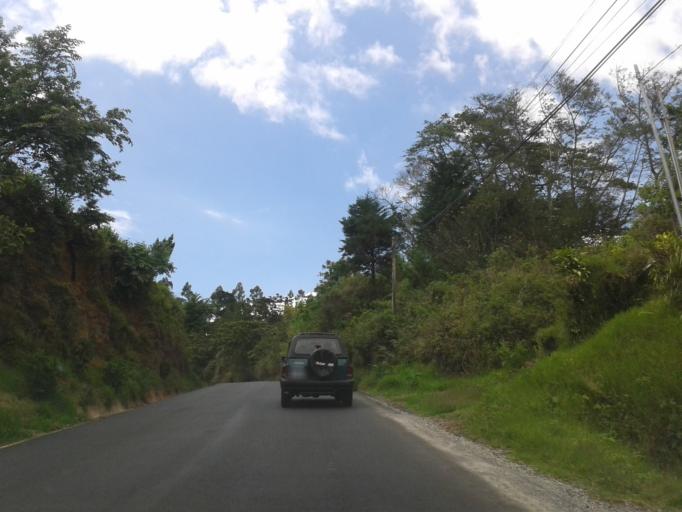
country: CR
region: Alajuela
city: Sabanilla
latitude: 10.1196
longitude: -84.1899
